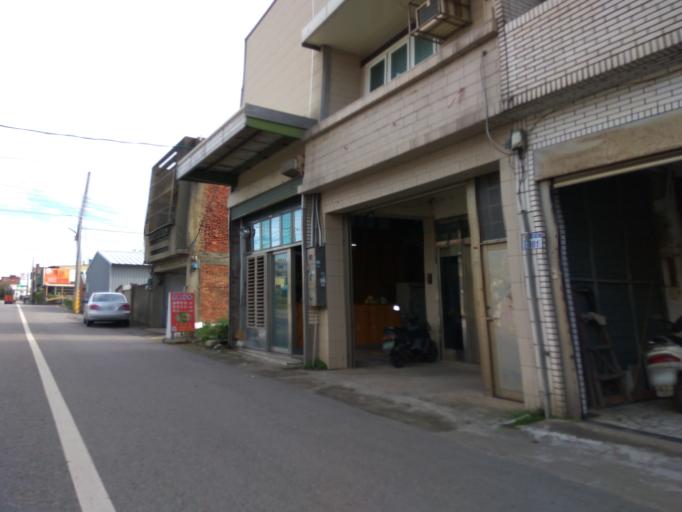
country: TW
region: Taiwan
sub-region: Hsinchu
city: Zhubei
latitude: 24.9650
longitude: 121.0972
